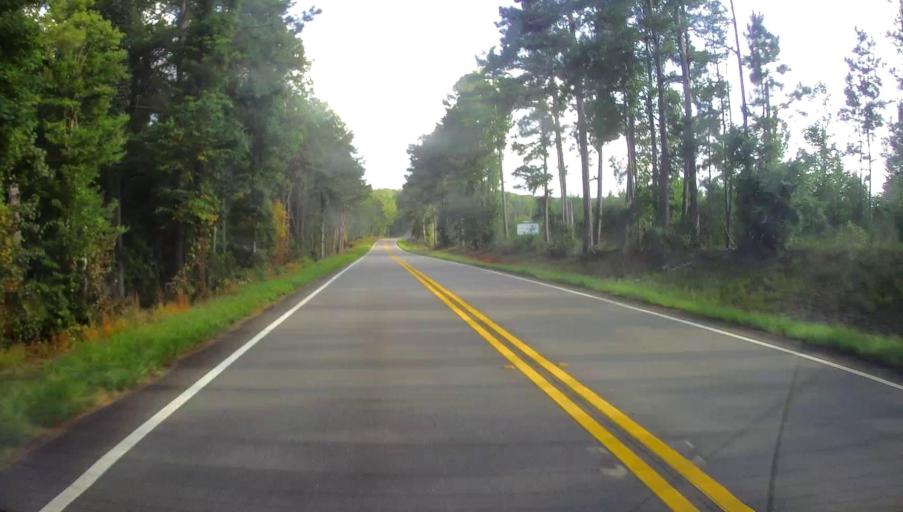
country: US
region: Georgia
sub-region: Monroe County
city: Forsyth
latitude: 32.9525
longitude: -83.9574
